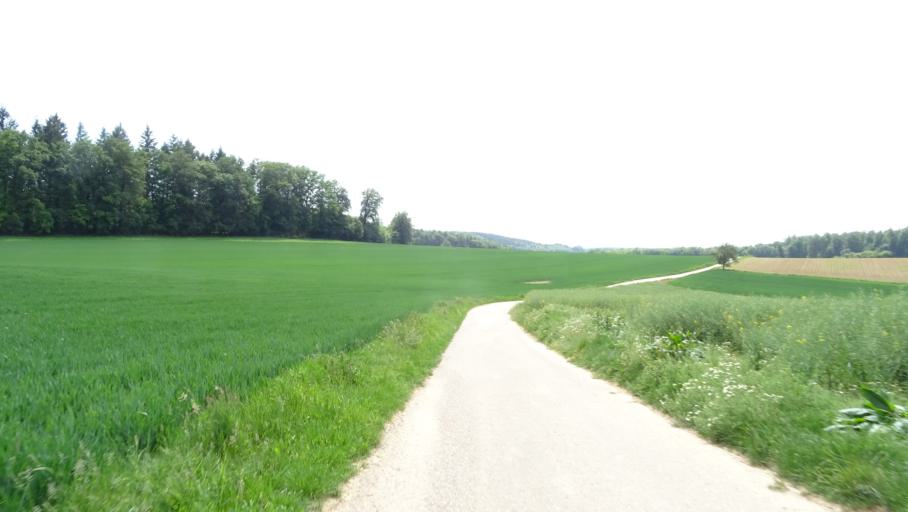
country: DE
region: Baden-Wuerttemberg
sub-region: Karlsruhe Region
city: Binau
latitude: 49.3772
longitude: 9.0475
